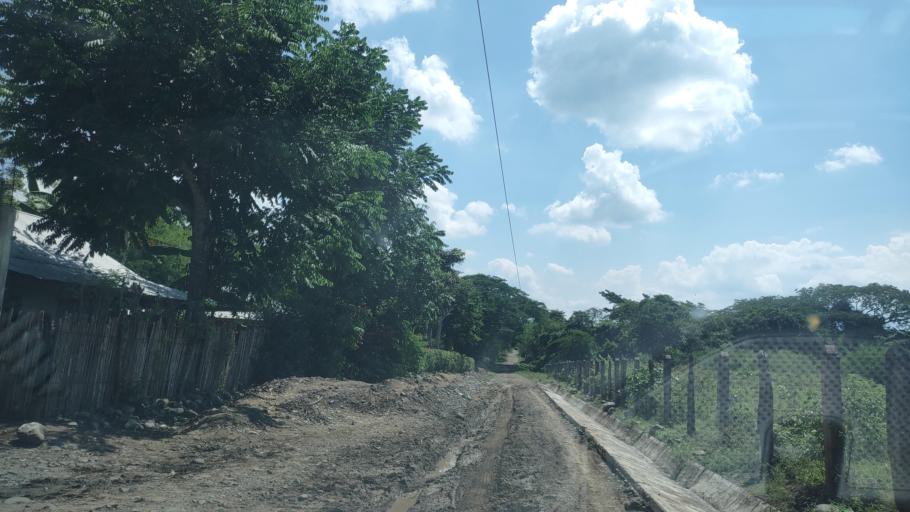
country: MX
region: Veracruz
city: Los Altos
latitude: 21.4302
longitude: -97.7916
